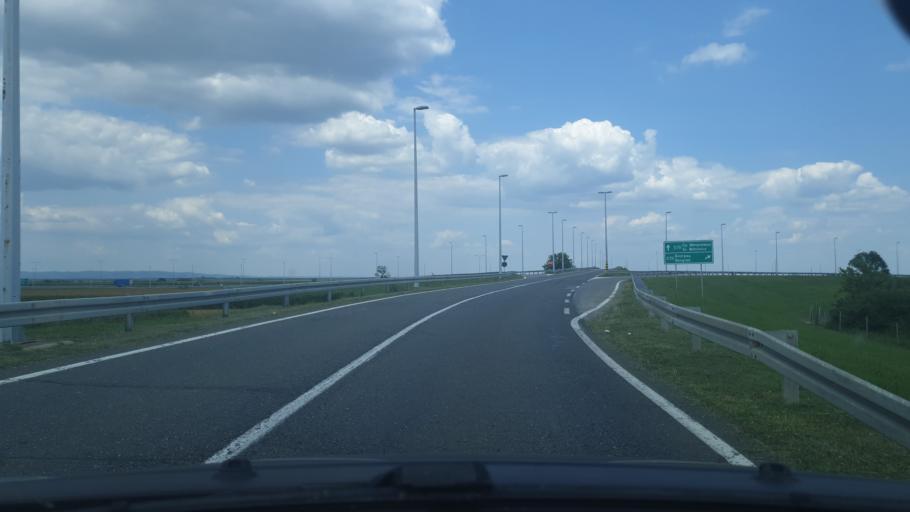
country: RS
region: Autonomna Pokrajina Vojvodina
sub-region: Sremski Okrug
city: Pecinci
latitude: 44.9212
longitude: 19.9492
